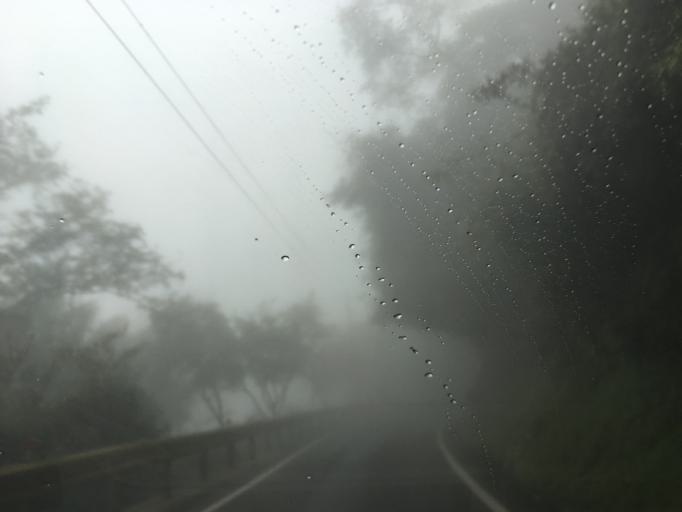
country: TW
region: Taiwan
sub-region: Hualien
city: Hualian
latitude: 24.1890
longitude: 121.4207
